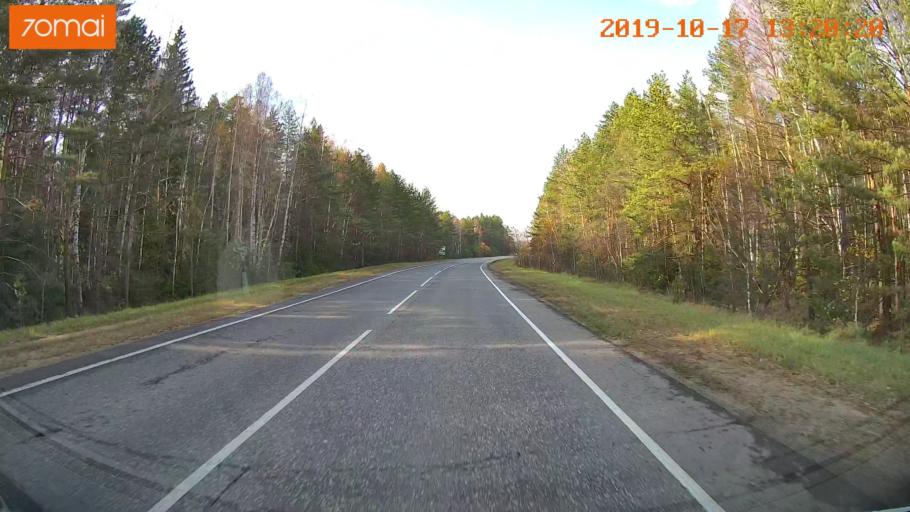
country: RU
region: Rjazan
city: Gus'-Zheleznyy
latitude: 55.0752
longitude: 41.0525
